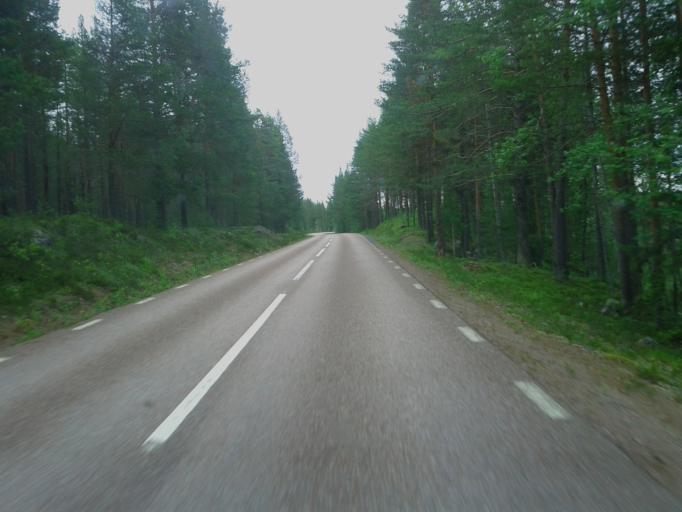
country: NO
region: Hedmark
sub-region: Trysil
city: Innbygda
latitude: 61.8350
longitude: 12.8281
